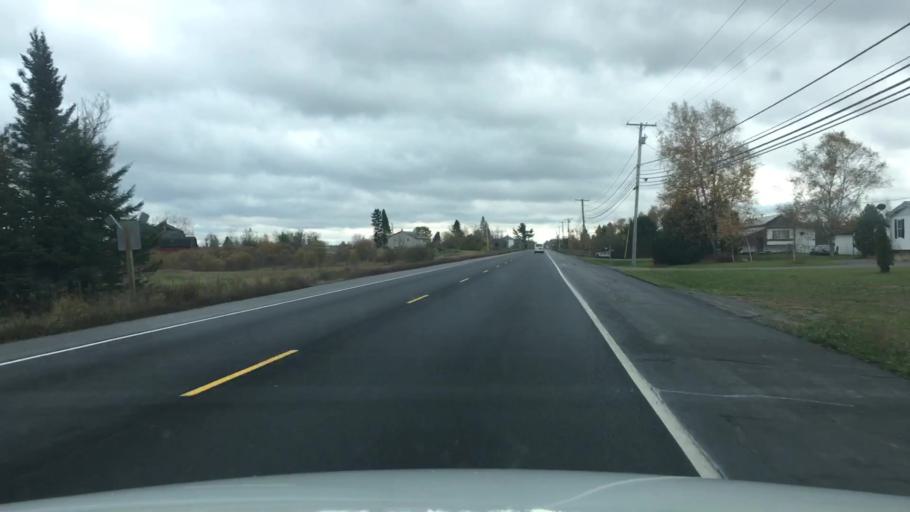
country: US
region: Maine
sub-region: Aroostook County
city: Houlton
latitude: 46.2537
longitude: -67.8408
